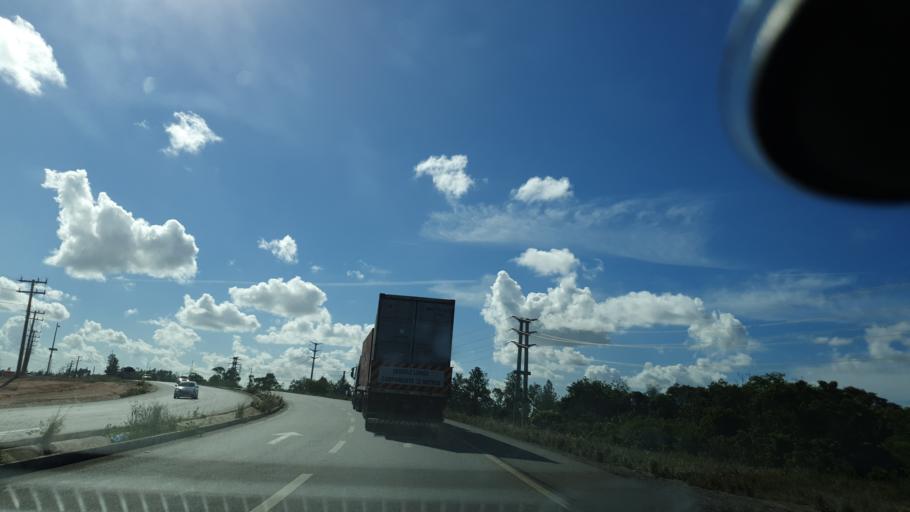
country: BR
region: Bahia
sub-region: Camacari
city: Camacari
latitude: -12.6833
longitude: -38.2656
